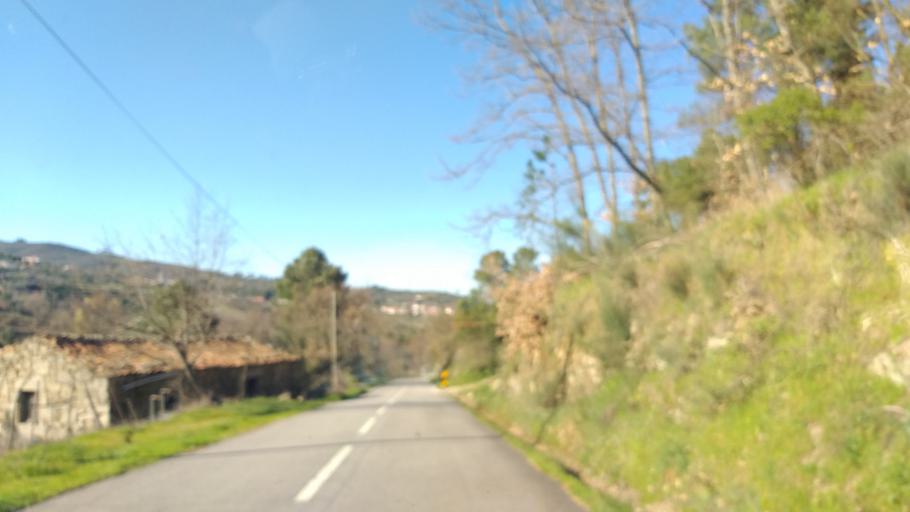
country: PT
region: Guarda
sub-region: Celorico da Beira
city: Celorico da Beira
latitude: 40.5939
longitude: -7.3625
